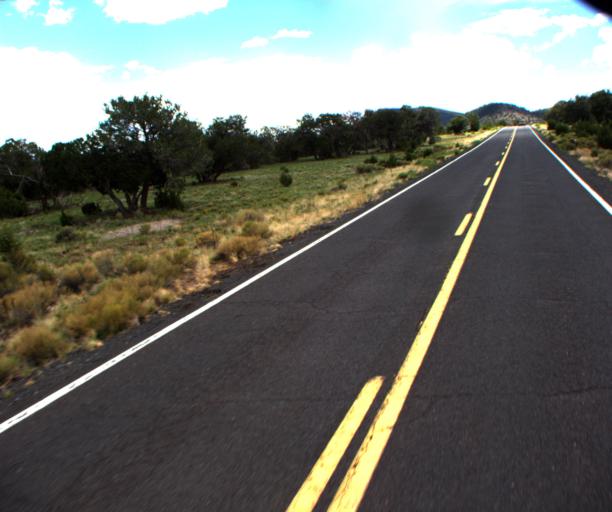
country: US
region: Arizona
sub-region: Coconino County
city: Parks
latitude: 35.5285
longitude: -111.8445
